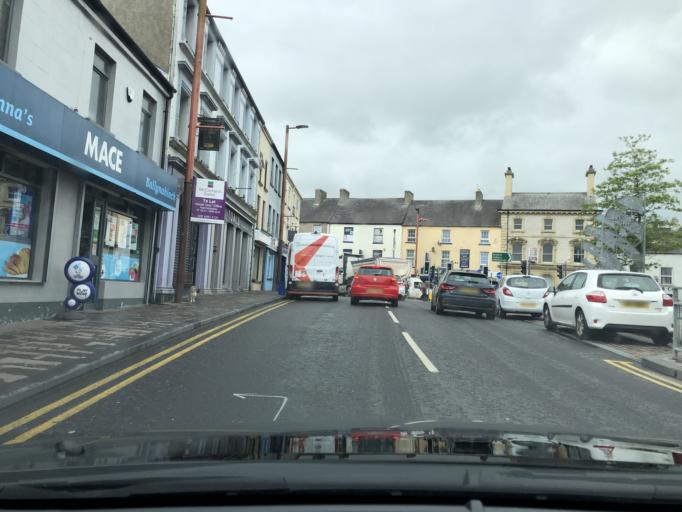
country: GB
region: Northern Ireland
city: Ballynahinch
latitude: 54.4018
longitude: -5.8966
